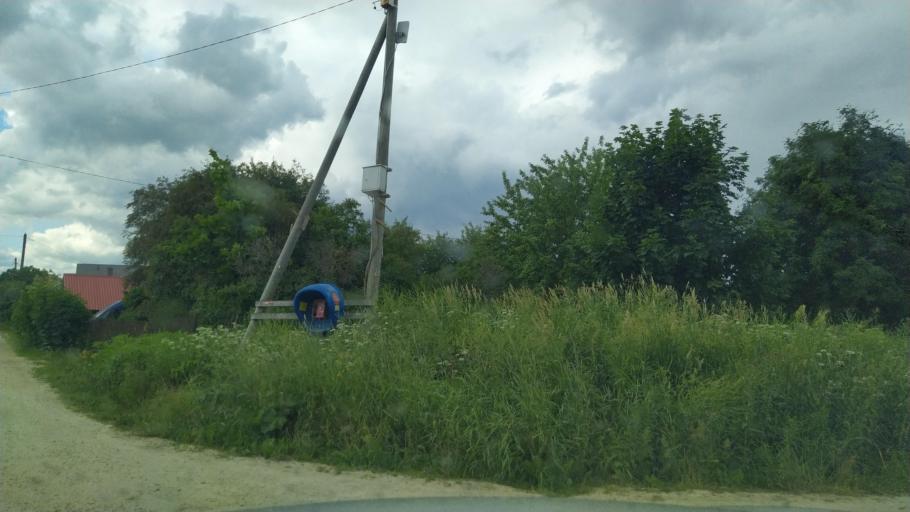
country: RU
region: Leningrad
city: Yelizavetino
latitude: 59.4201
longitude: 29.7776
